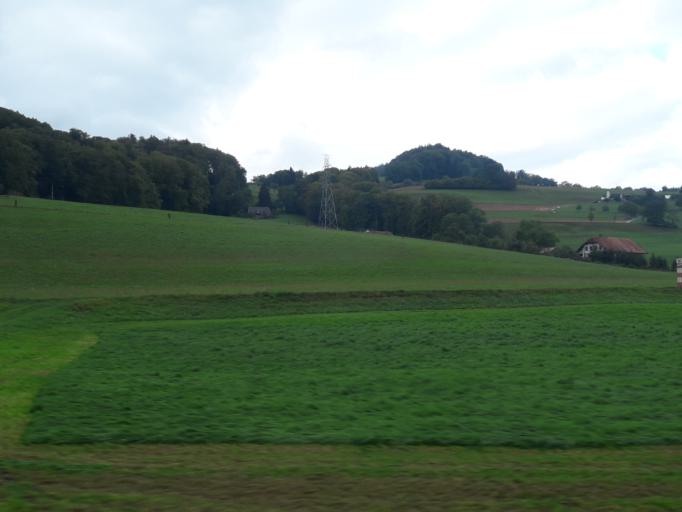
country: CH
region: Bern
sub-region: Bern-Mittelland District
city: Muhlethurnen
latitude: 46.8037
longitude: 7.5165
